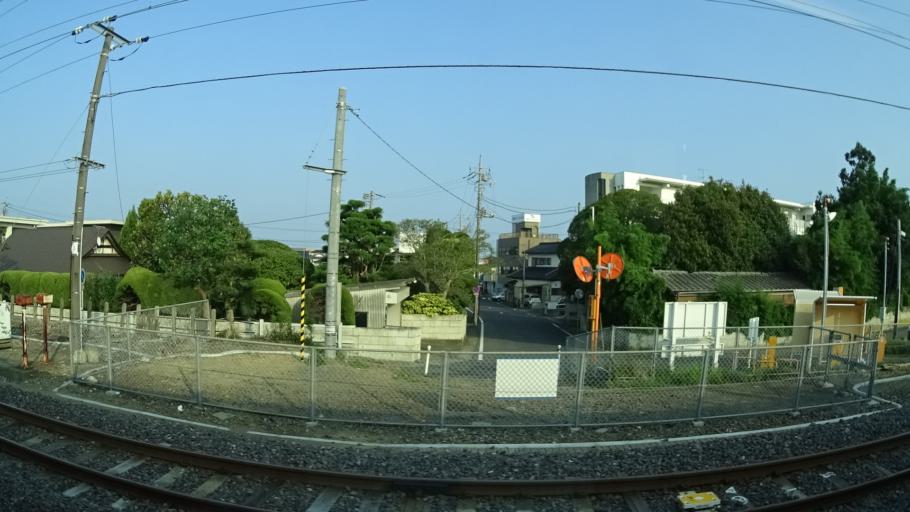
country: JP
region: Ibaraki
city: Hitachi
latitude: 36.5507
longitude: 140.6308
